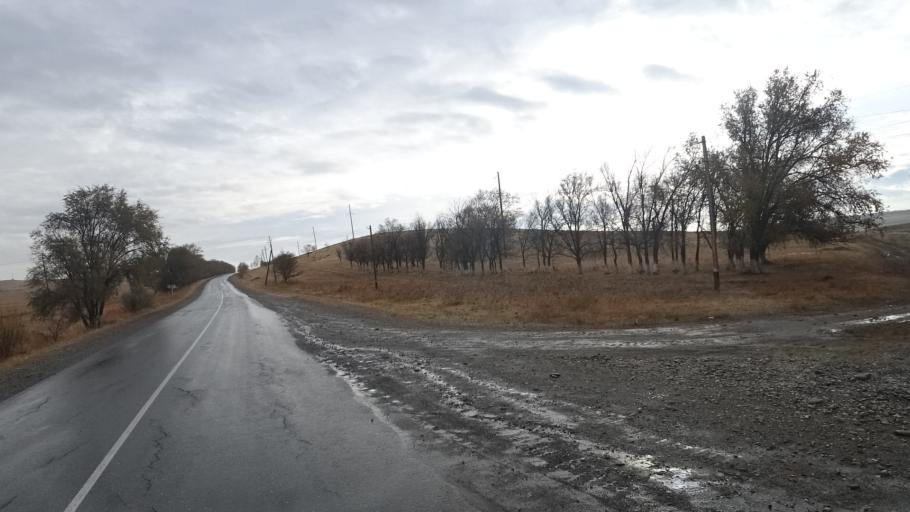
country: KZ
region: Ongtustik Qazaqstan
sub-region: Tulkibas Audany
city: Zhabagly
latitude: 42.5161
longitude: 70.5097
